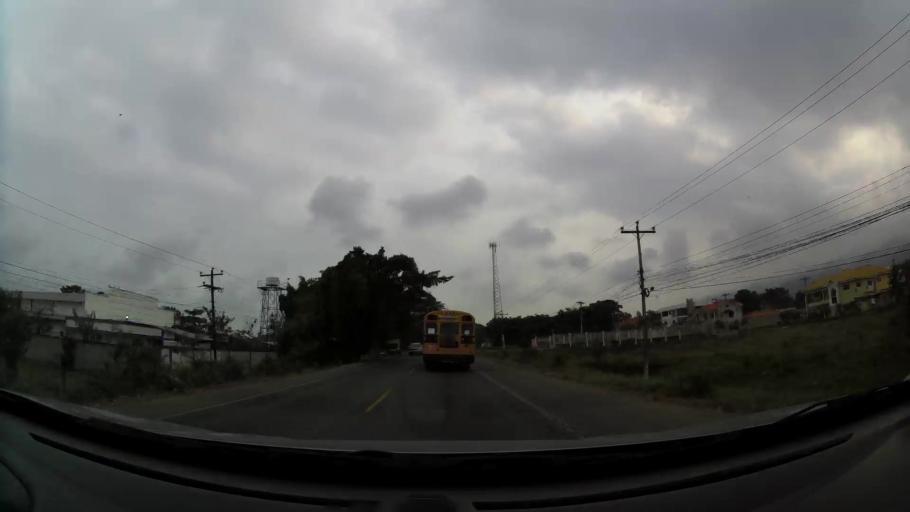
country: HN
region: Yoro
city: El Progreso
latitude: 15.4376
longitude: -87.7935
